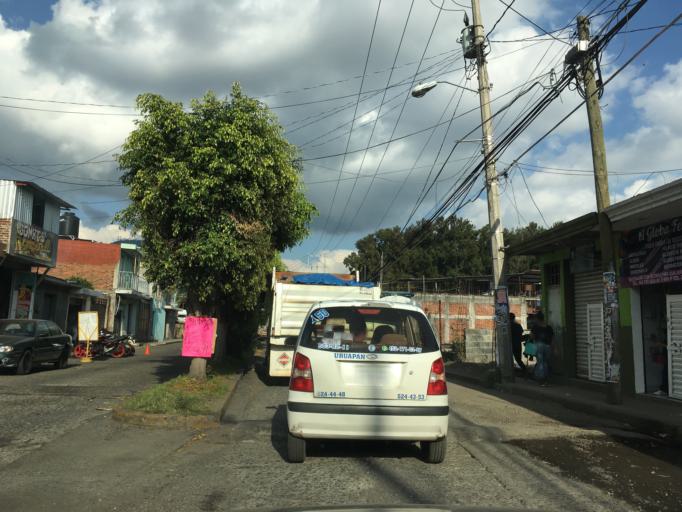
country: MX
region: Michoacan
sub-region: Uruapan
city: Uruapan
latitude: 19.4309
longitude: -102.0763
